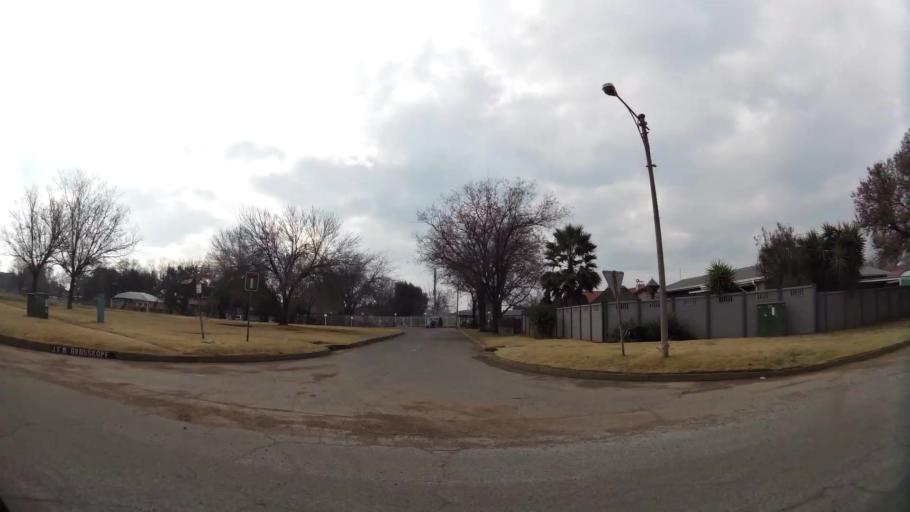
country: ZA
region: Gauteng
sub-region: Sedibeng District Municipality
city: Vanderbijlpark
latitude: -26.6831
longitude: 27.8330
